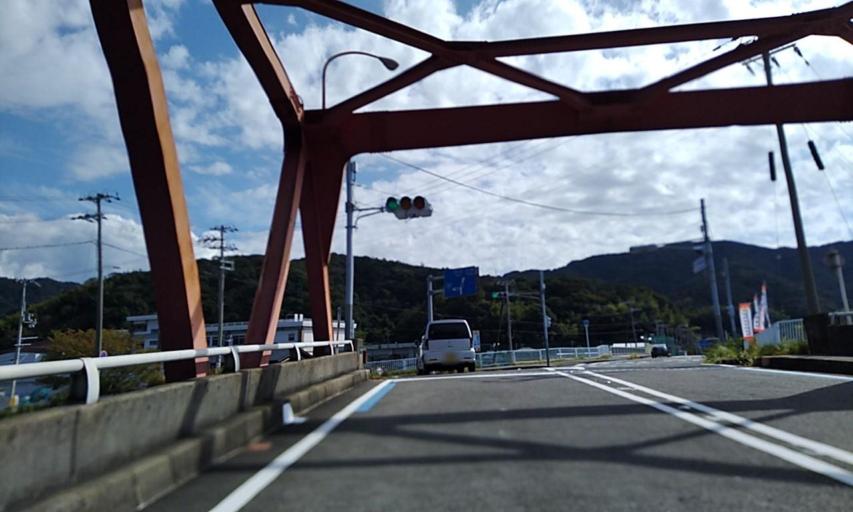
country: JP
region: Wakayama
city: Gobo
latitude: 33.9598
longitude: 135.1150
